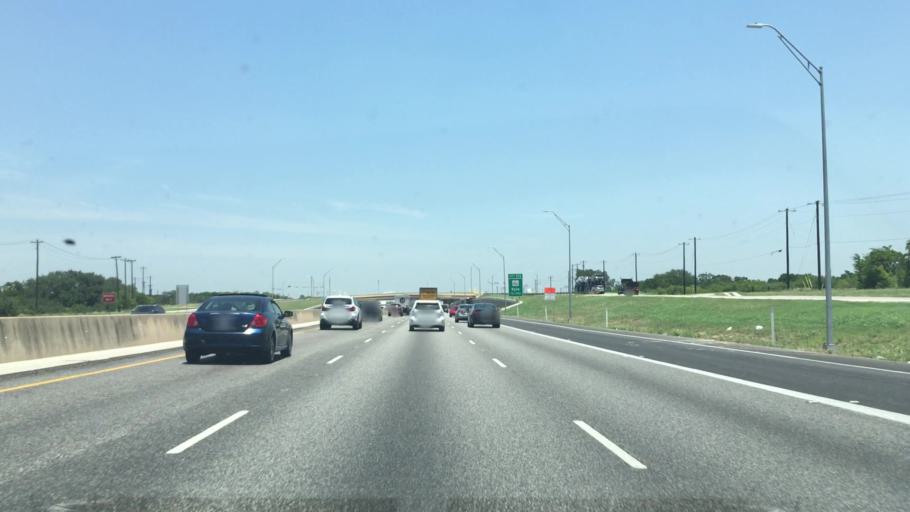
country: US
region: Texas
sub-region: Hays County
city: Kyle
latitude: 29.9432
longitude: -97.8823
